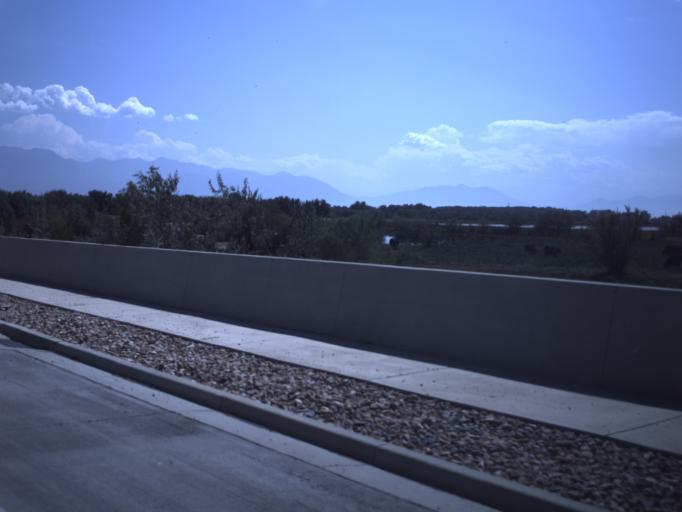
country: US
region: Utah
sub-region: Utah County
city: Saratoga Springs
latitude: 40.3762
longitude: -111.8994
